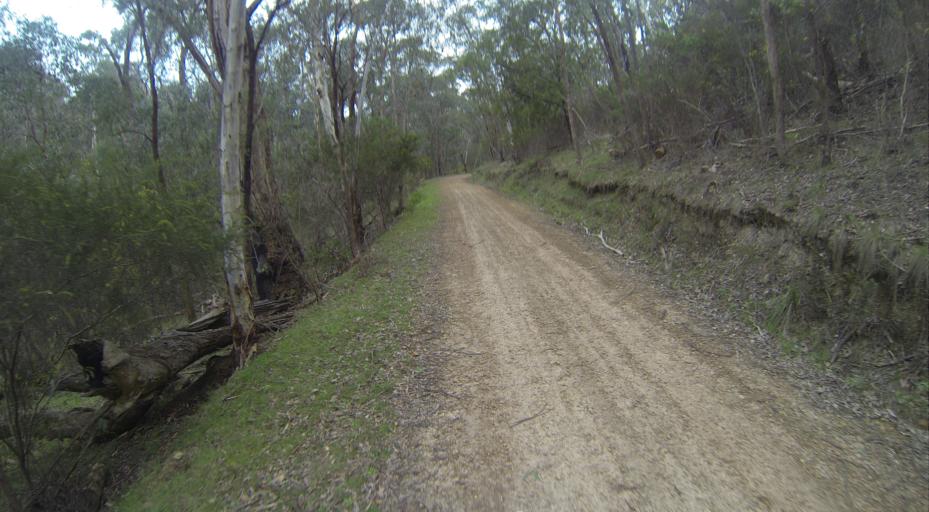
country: AU
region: Victoria
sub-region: Nillumbik
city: Saint Andrews
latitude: -37.6470
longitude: 145.2938
